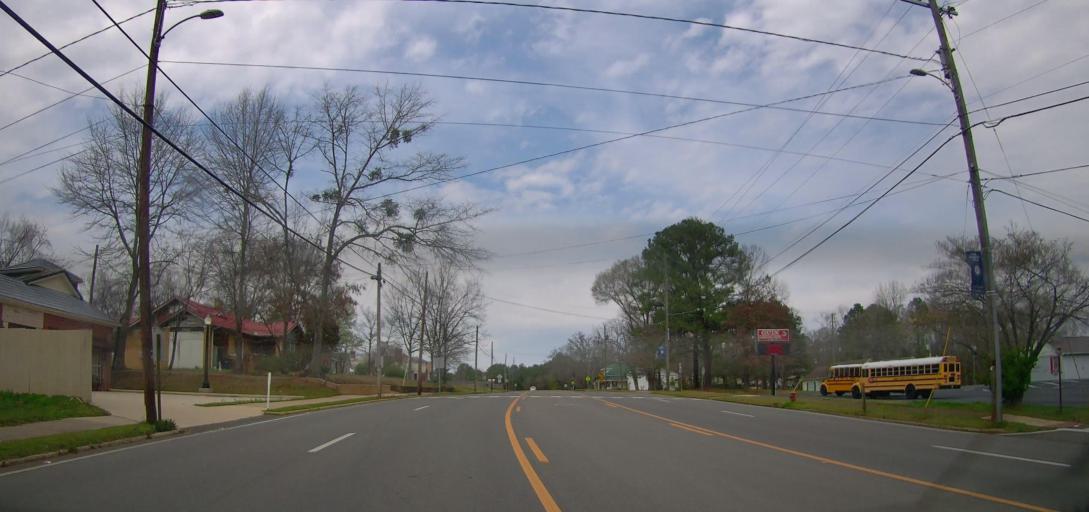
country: US
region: Alabama
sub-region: Marion County
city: Guin
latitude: 33.9717
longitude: -87.9157
